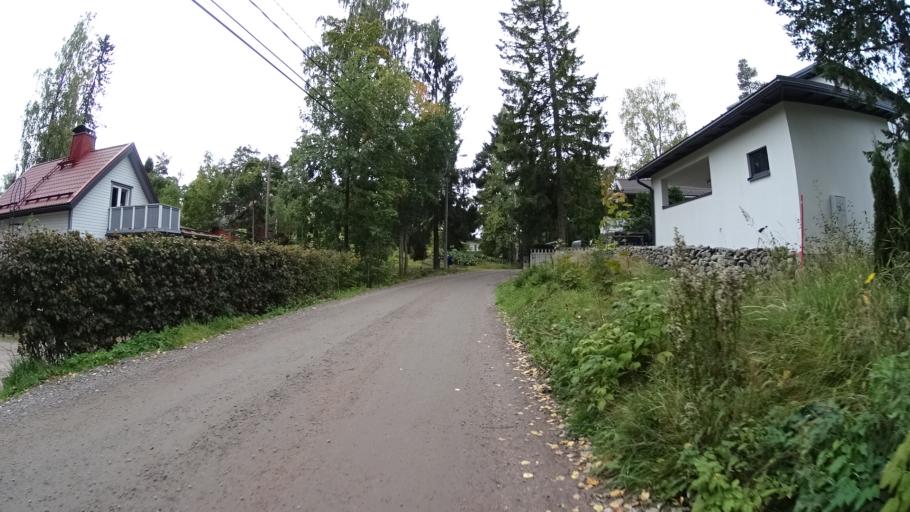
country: FI
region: Uusimaa
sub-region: Helsinki
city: Kauniainen
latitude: 60.2230
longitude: 24.7368
